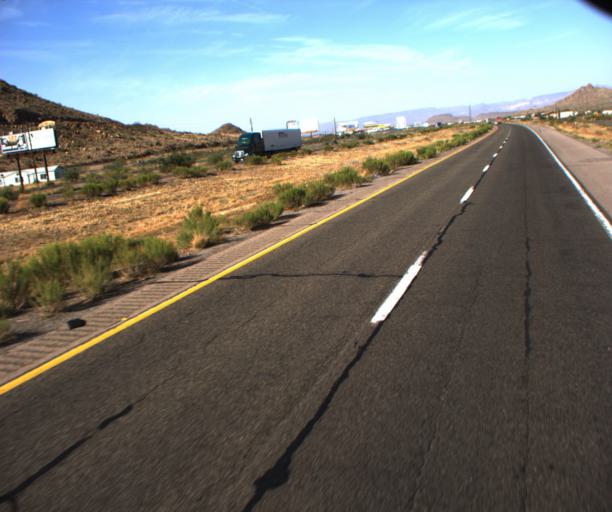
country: US
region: Arizona
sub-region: Mohave County
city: Kingman
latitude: 35.1604
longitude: -114.0785
